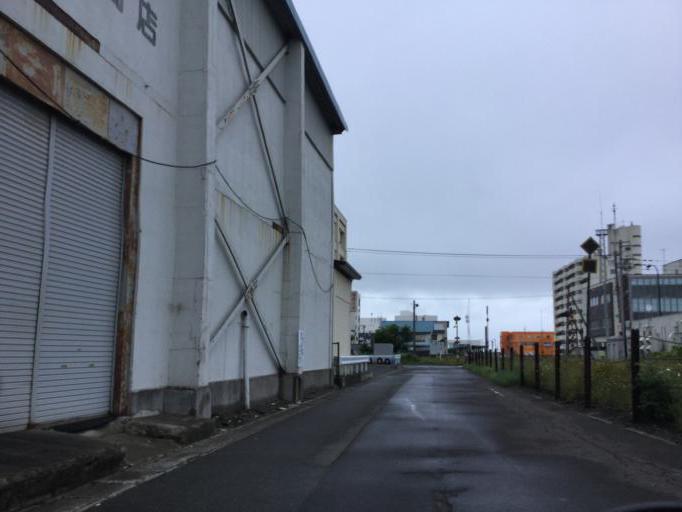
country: JP
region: Hokkaido
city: Wakkanai
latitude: 45.4141
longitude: 141.6769
